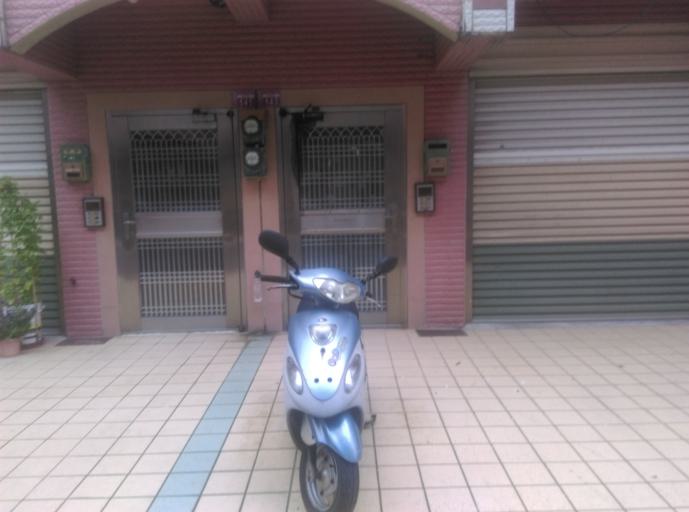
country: TW
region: Taiwan
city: Taoyuan City
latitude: 24.9989
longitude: 121.2528
